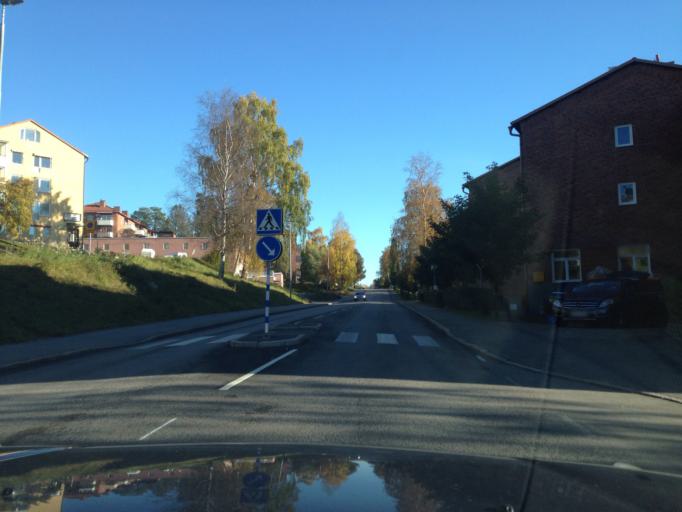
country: SE
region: Vaesternorrland
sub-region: Sundsvalls Kommun
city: Sundsvall
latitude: 62.3972
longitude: 17.3182
